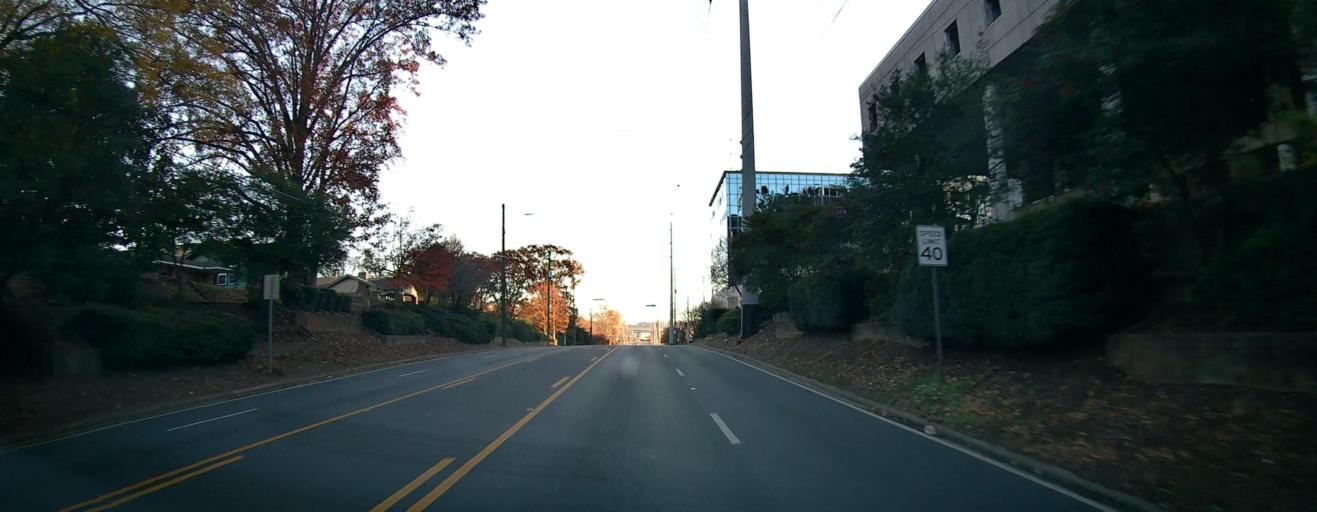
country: US
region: Alabama
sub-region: Jefferson County
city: Birmingham
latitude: 33.5375
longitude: -86.8104
